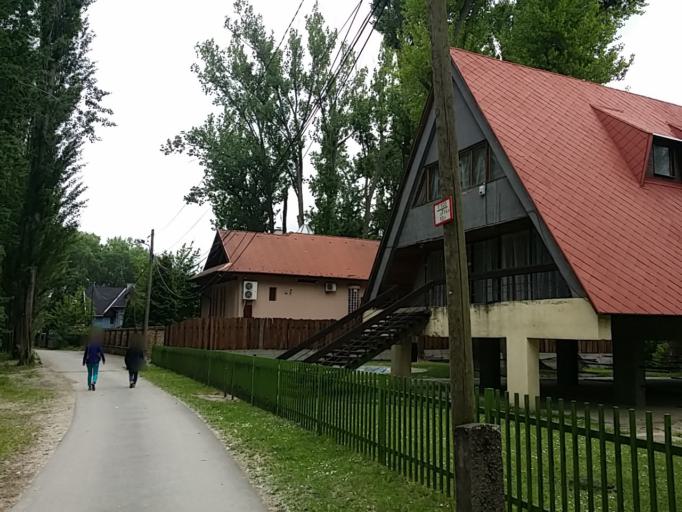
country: HU
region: Pest
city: Szentendre
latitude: 47.6790
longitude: 19.0824
